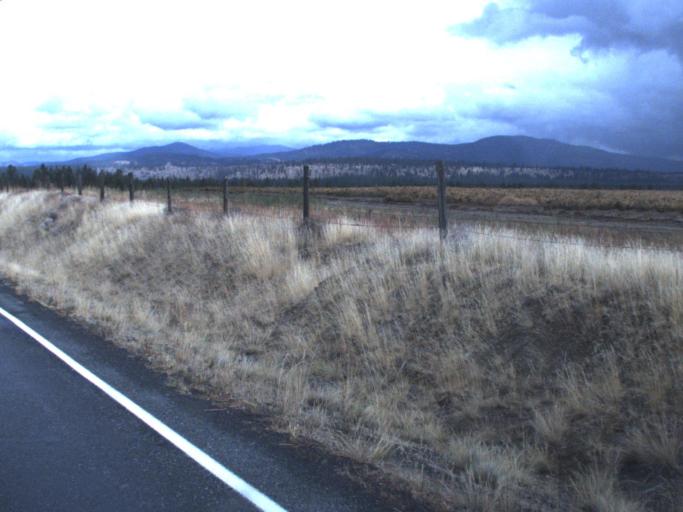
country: US
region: Washington
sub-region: Spokane County
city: Fairchild Air Force Base
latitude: 47.8311
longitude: -117.8758
